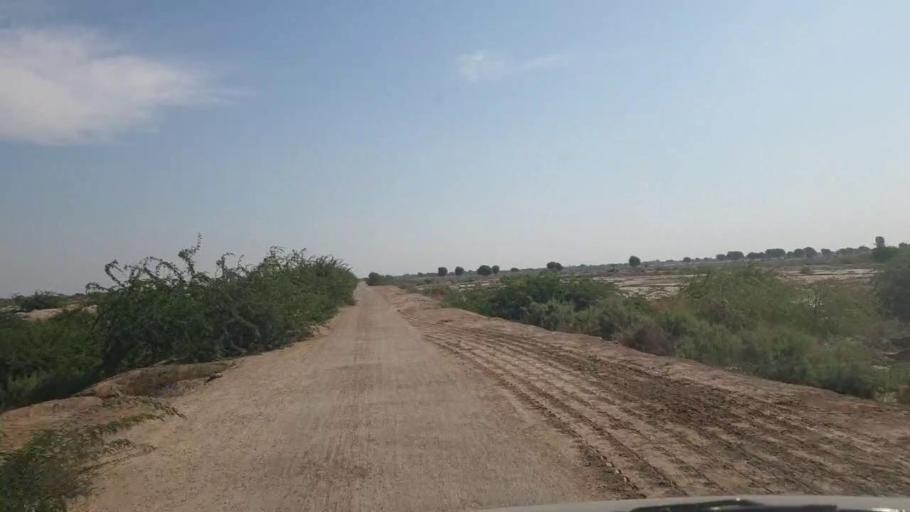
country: PK
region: Sindh
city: Digri
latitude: 24.9641
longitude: 69.1217
